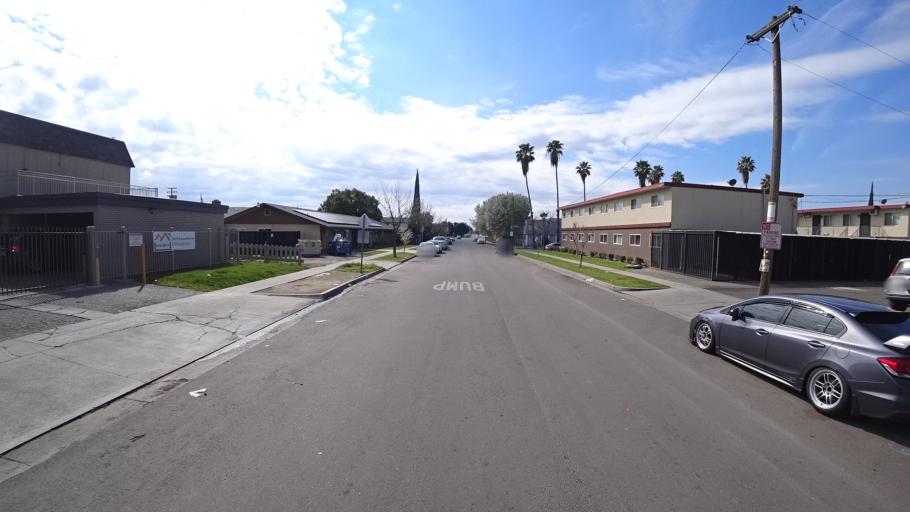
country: US
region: California
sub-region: Fresno County
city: Clovis
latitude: 36.8137
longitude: -119.7631
